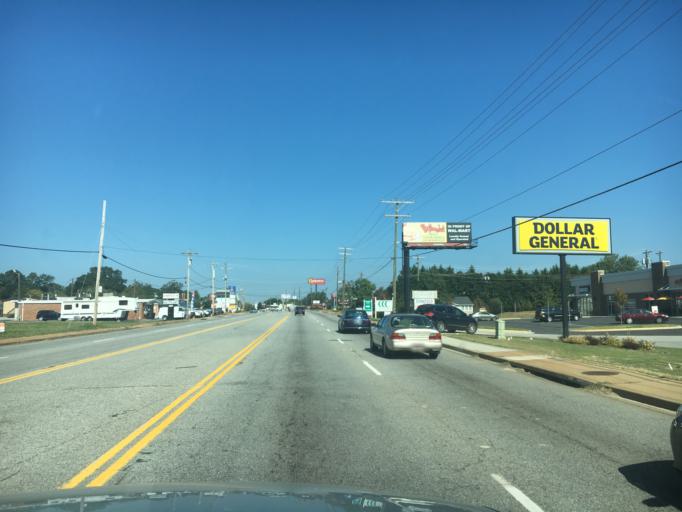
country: US
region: South Carolina
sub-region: Spartanburg County
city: Boiling Springs
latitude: 35.0379
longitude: -81.9736
